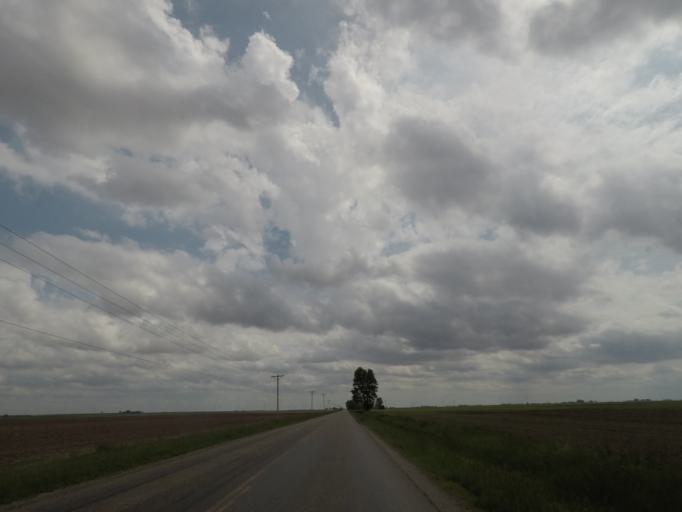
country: US
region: Illinois
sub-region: De Witt County
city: Clinton
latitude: 40.0927
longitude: -89.0859
